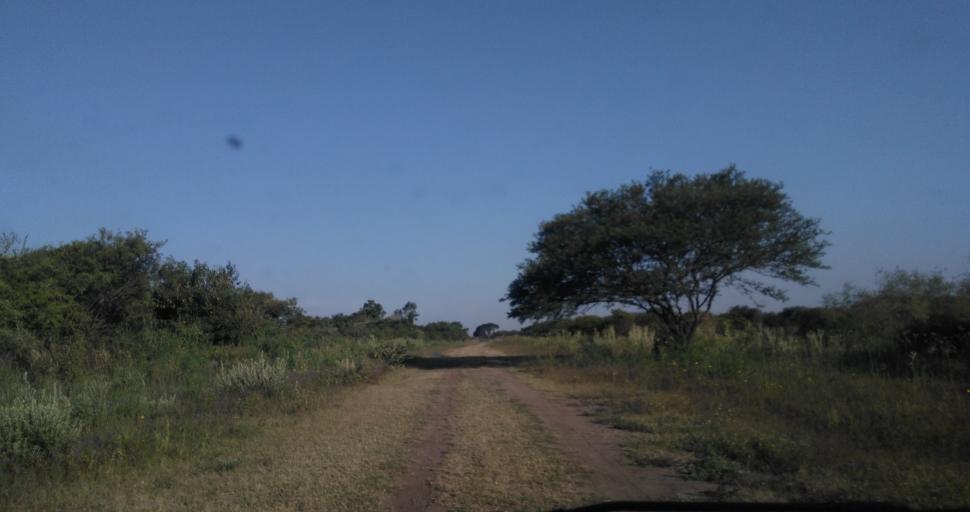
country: AR
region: Chaco
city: Fontana
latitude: -27.4282
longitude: -59.0526
